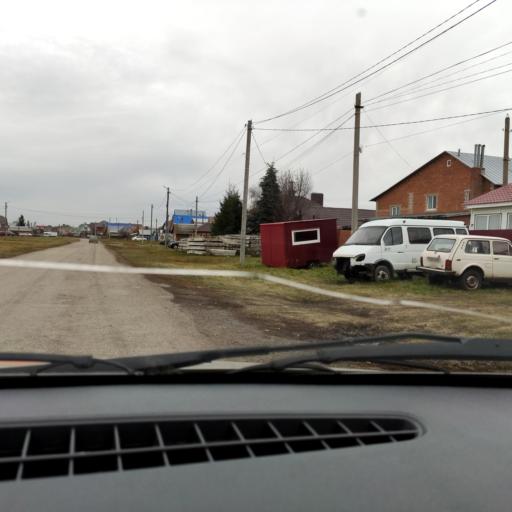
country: RU
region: Bashkortostan
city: Ufa
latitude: 54.8344
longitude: 56.0021
